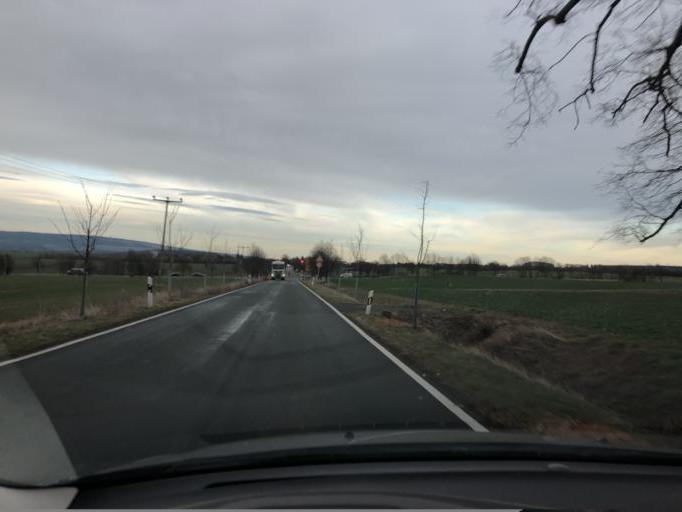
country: DE
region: Thuringia
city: Monchenholzhausen
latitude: 50.9560
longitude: 11.1599
